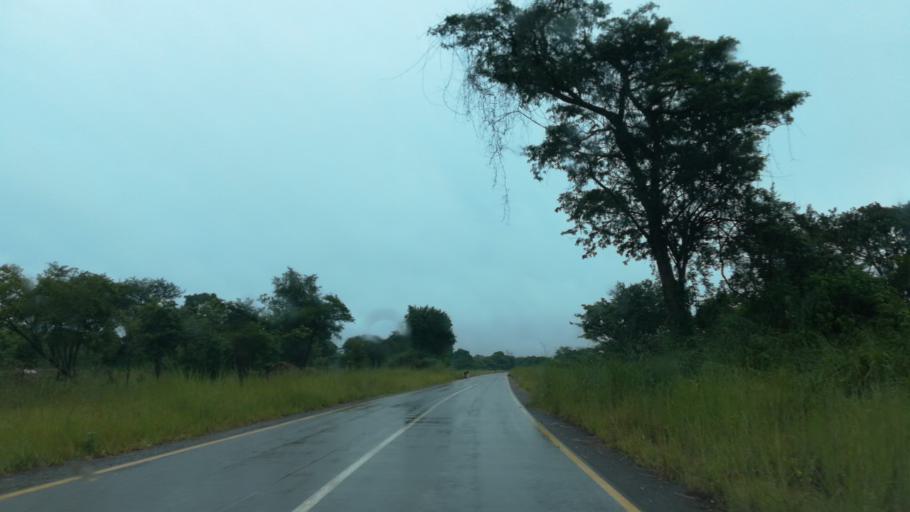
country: ZM
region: Luapula
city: Mwense
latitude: -10.8526
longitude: 28.2253
